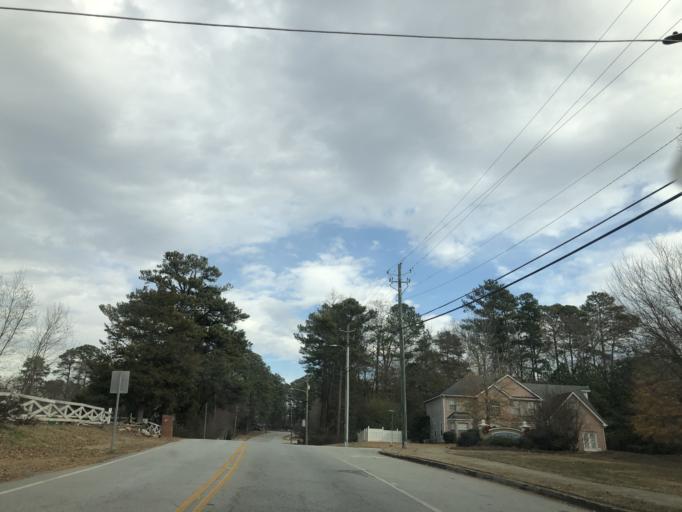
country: US
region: Georgia
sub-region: DeKalb County
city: Panthersville
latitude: 33.6642
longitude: -84.2034
